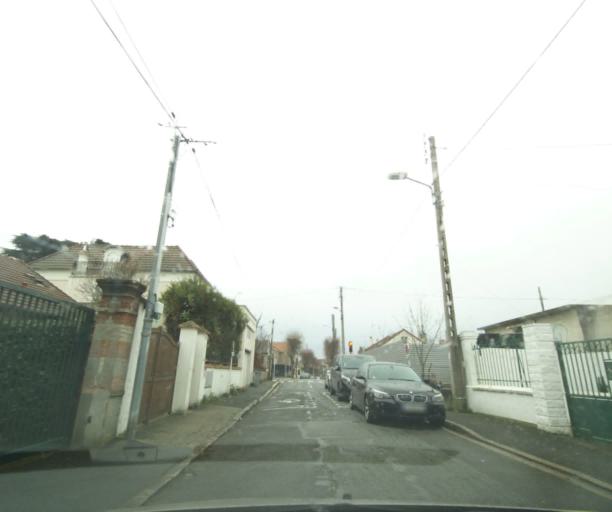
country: FR
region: Ile-de-France
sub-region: Departement du Val-de-Marne
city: Ablon-sur-Seine
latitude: 48.7315
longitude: 2.4212
